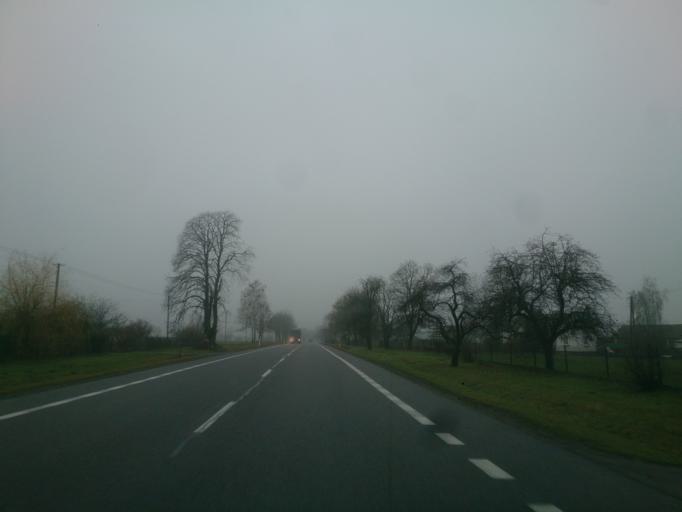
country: PL
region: Masovian Voivodeship
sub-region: Powiat plonski
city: Dzierzaznia
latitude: 52.6247
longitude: 20.2686
